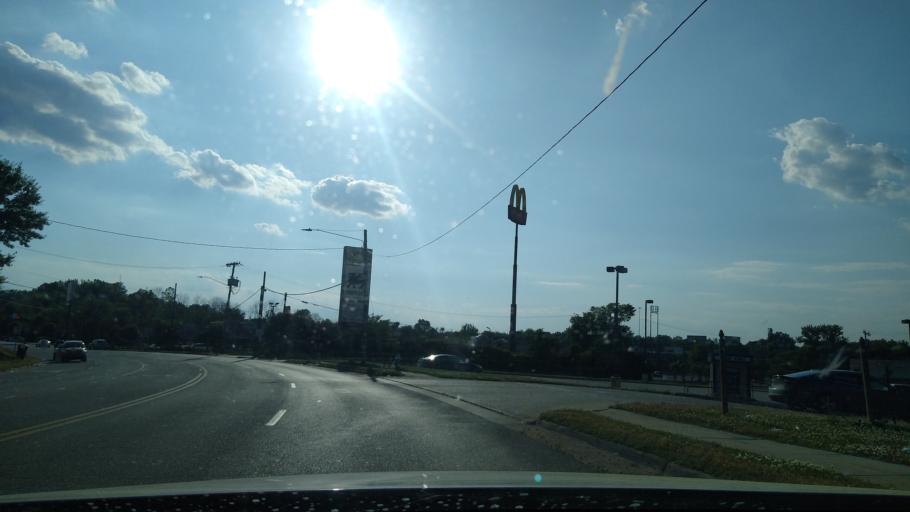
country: US
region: North Carolina
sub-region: Guilford County
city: Greensboro
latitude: 36.0415
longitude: -79.7708
